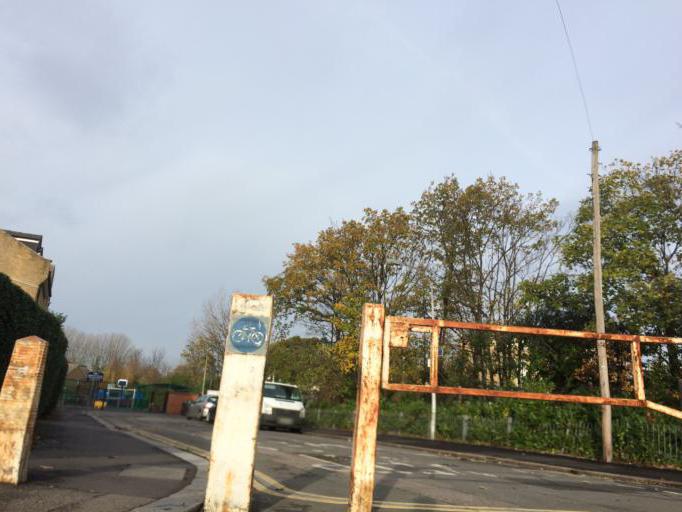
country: GB
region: England
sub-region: Greater London
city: Walthamstow
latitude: 51.5810
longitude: -0.0235
